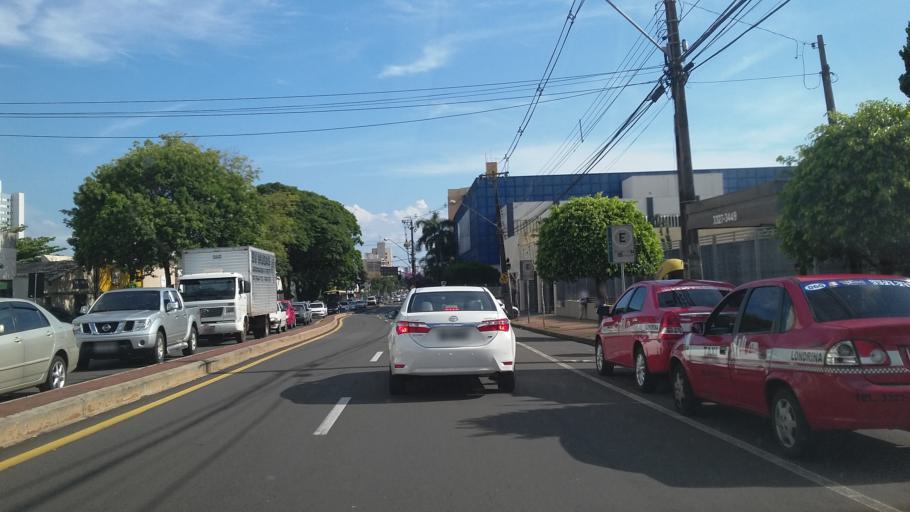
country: BR
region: Parana
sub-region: Londrina
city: Londrina
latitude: -23.3017
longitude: -51.1792
